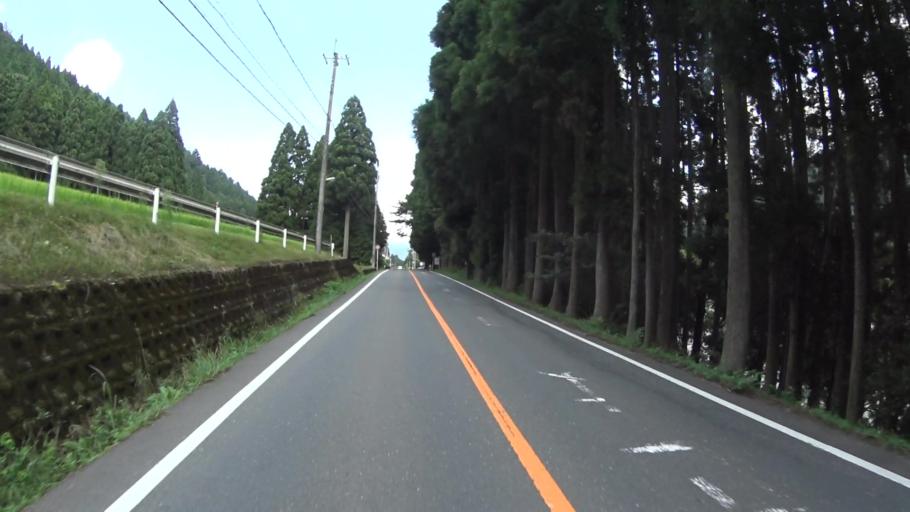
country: JP
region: Shiga Prefecture
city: Kitahama
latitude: 35.3285
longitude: 135.8986
